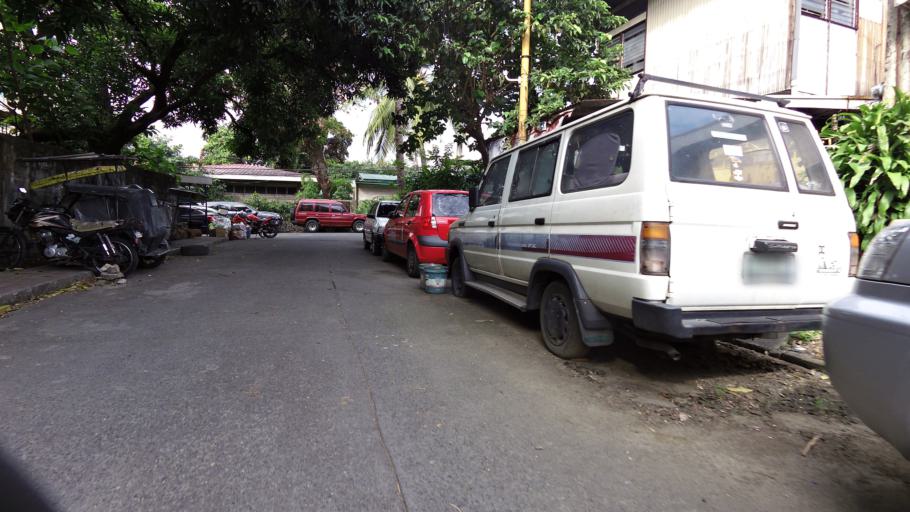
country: PH
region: Metro Manila
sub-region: Pasig
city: Pasig City
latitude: 14.5664
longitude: 121.0616
